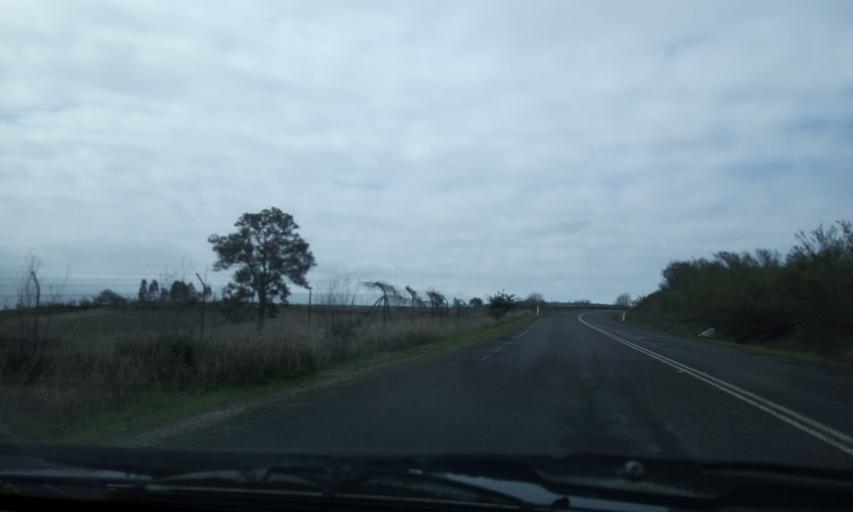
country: AU
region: New South Wales
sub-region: Camden
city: Camden South
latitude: -34.1299
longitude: 150.7151
